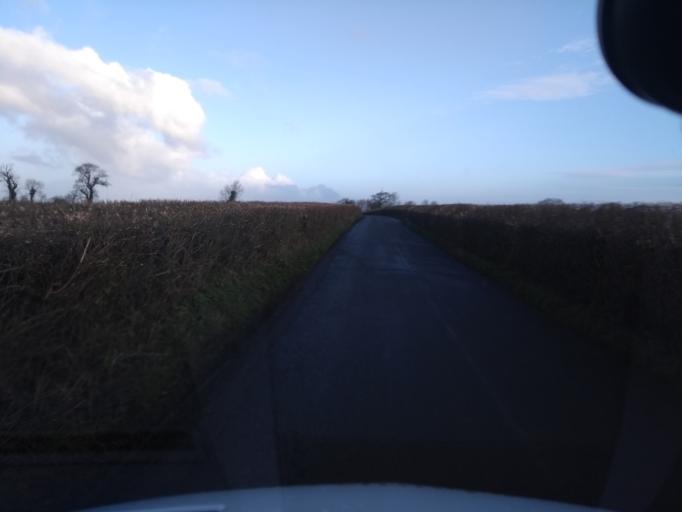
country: GB
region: England
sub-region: Somerset
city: Wedmore
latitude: 51.2329
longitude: -2.8160
